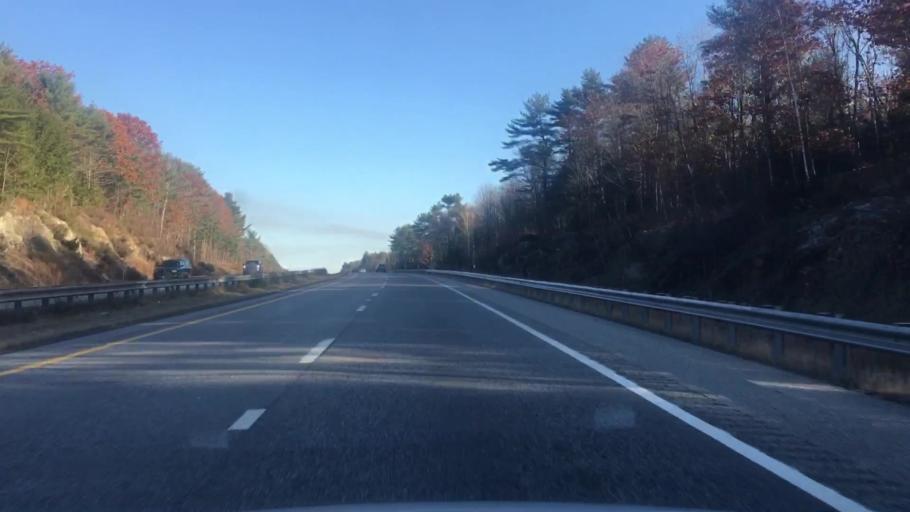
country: US
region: Maine
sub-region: Cumberland County
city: New Gloucester
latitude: 44.0155
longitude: -70.2969
